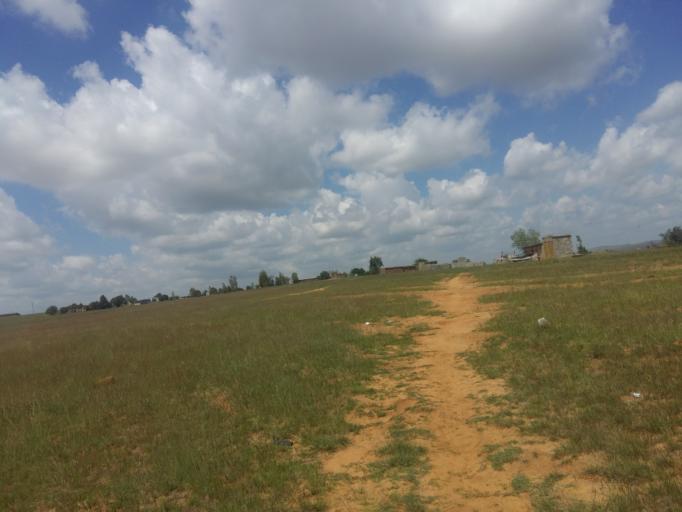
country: LS
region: Mafeteng
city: Mafeteng
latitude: -29.7494
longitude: 27.1141
